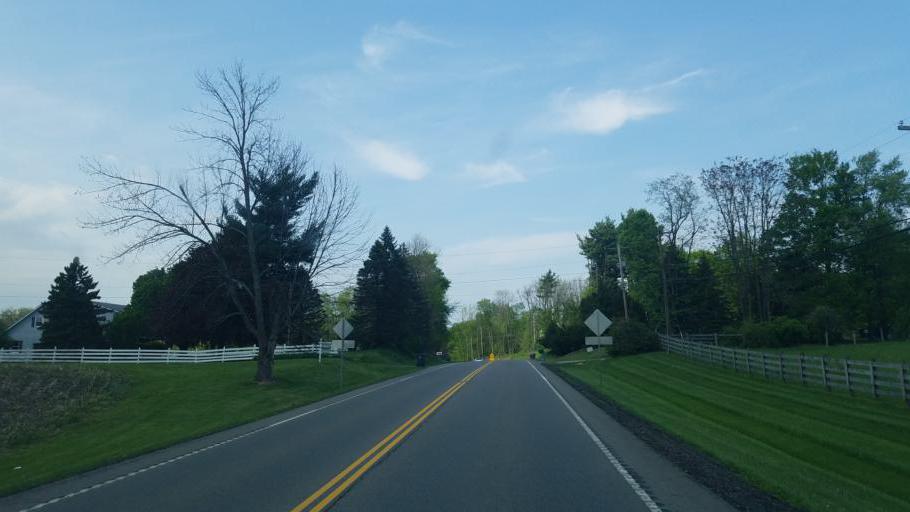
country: US
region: Ohio
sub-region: Licking County
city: Granville South
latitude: 40.0412
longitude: -82.5224
